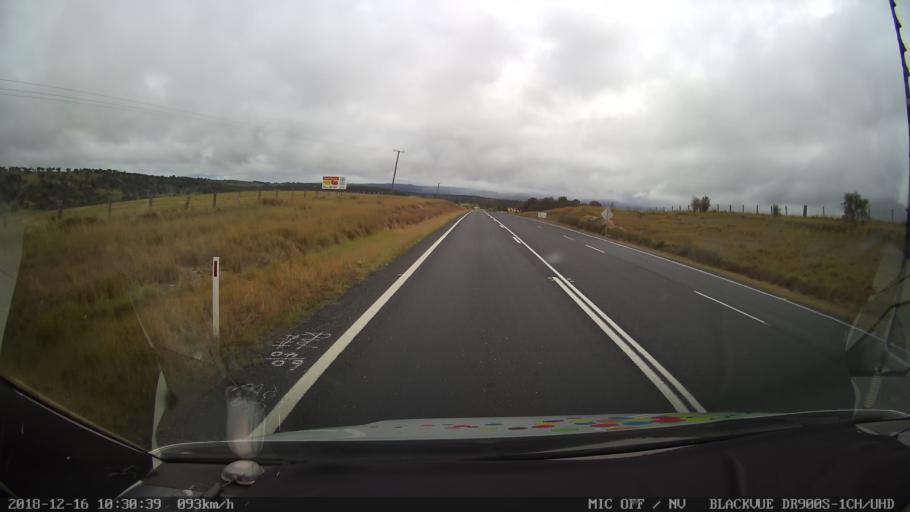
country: AU
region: New South Wales
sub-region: Tenterfield Municipality
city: Carrolls Creek
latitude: -29.0904
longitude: 152.0031
